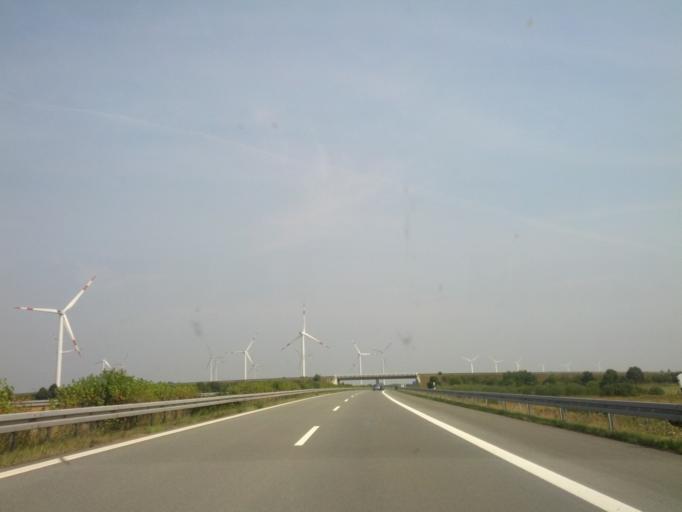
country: DE
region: Mecklenburg-Vorpommern
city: Grimmen
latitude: 54.0875
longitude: 12.9584
